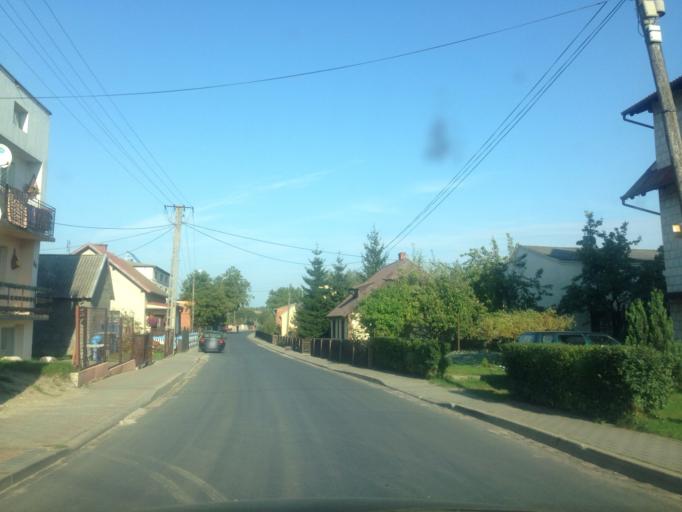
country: PL
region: Kujawsko-Pomorskie
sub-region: Powiat brodnicki
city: Brzozie
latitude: 53.3265
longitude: 19.6105
